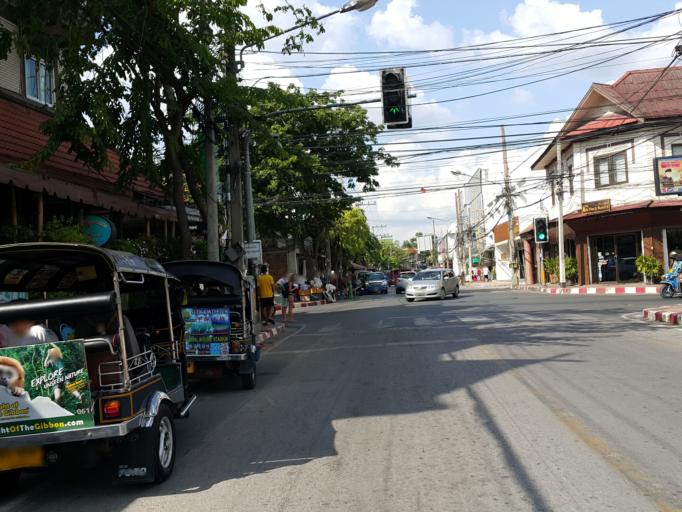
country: TH
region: Chiang Mai
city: Chiang Mai
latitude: 18.7878
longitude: 98.9880
